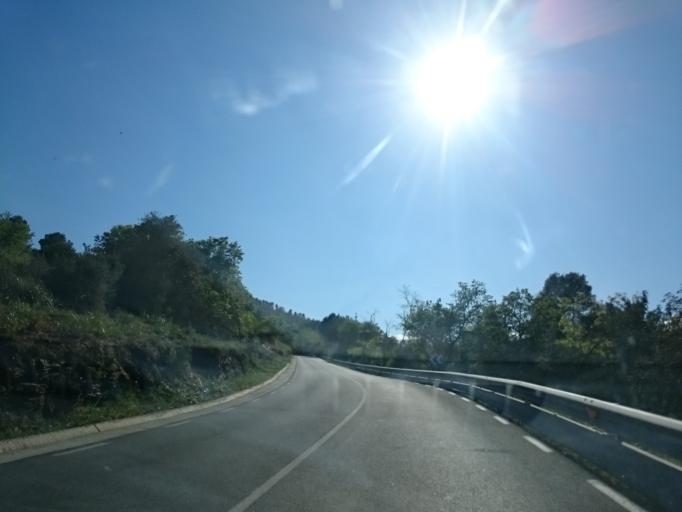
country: ES
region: Catalonia
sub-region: Provincia de Barcelona
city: Sant Boi de Llobregat
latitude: 41.3455
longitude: 2.0160
